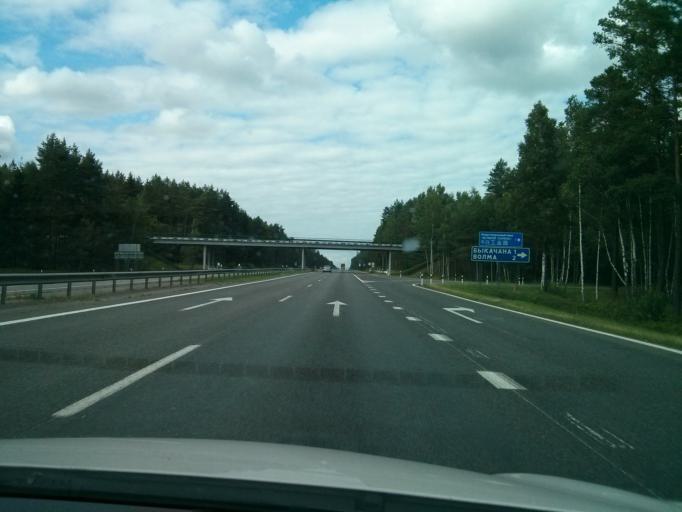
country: BY
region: Minsk
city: Zamostochcha
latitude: 53.8910
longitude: 27.9414
